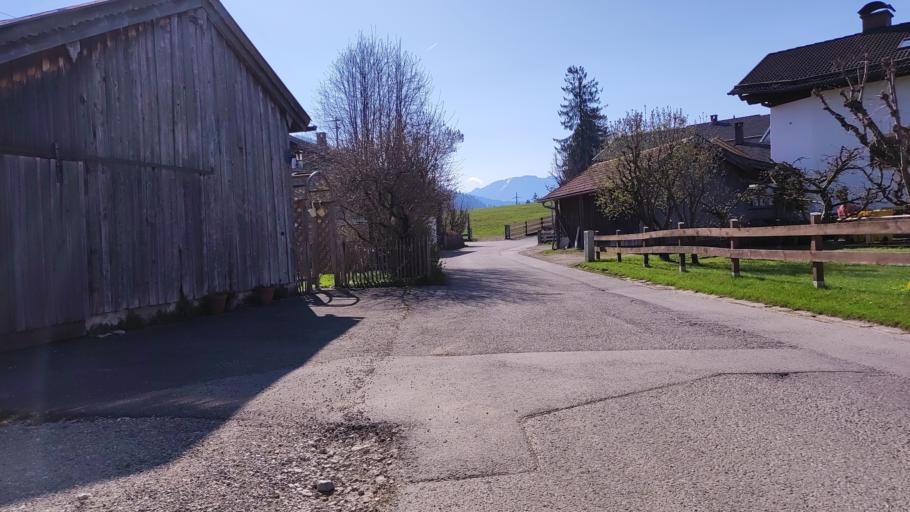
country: DE
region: Bavaria
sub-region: Upper Bavaria
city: Saulgrub
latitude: 47.6477
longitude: 11.0154
